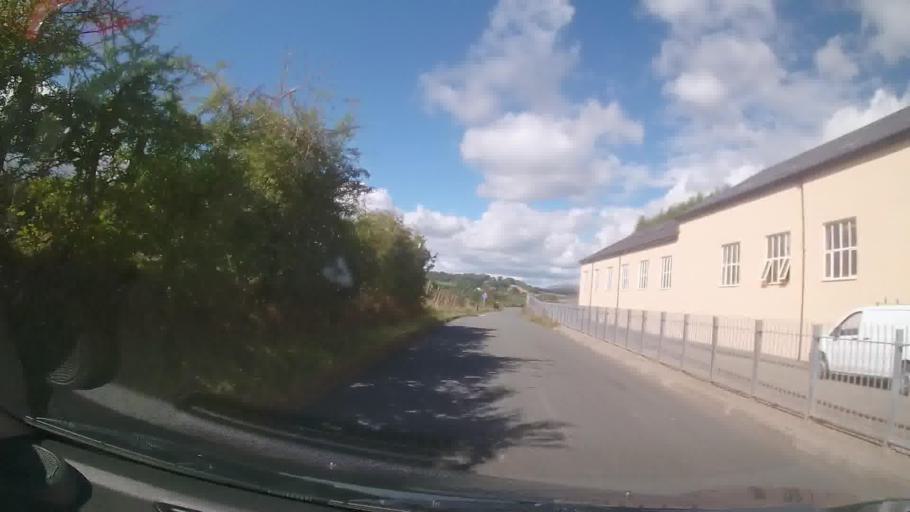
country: GB
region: Wales
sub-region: Merthyr Tydfil County Borough
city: Merthyr Tydfil
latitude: 51.7780
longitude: -3.3651
